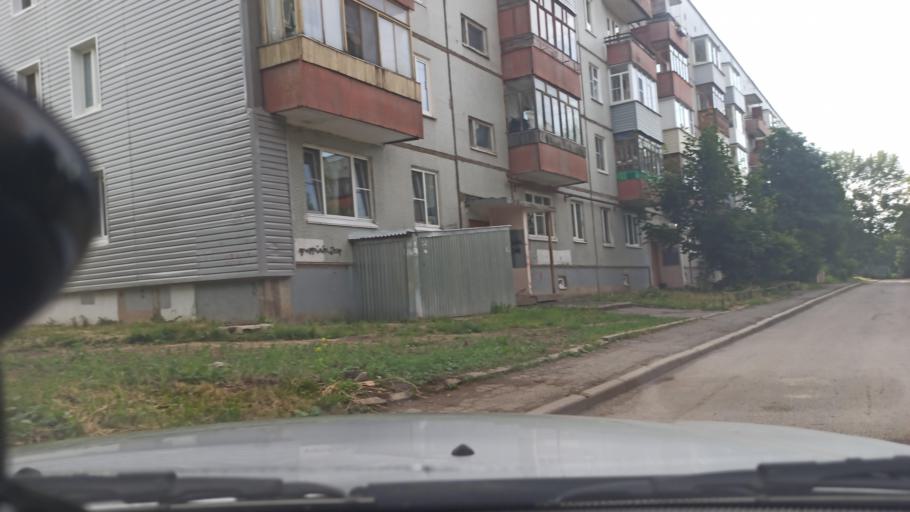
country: RU
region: Vologda
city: Vologda
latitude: 59.1864
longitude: 39.9070
